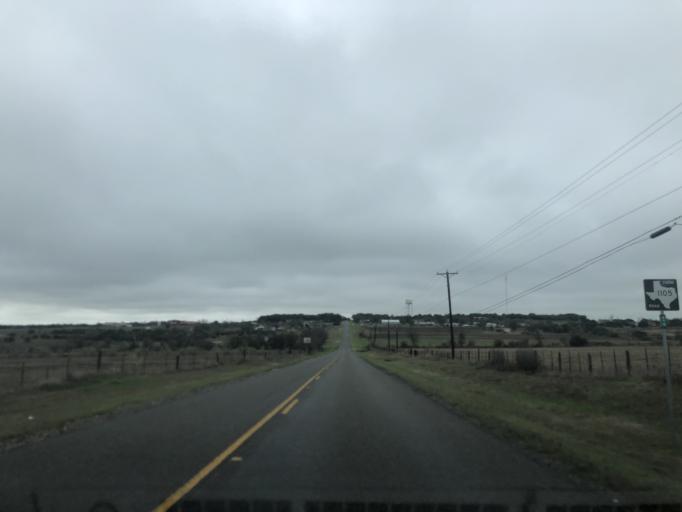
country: US
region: Texas
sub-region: Williamson County
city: Serenada
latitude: 30.7533
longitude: -97.6029
